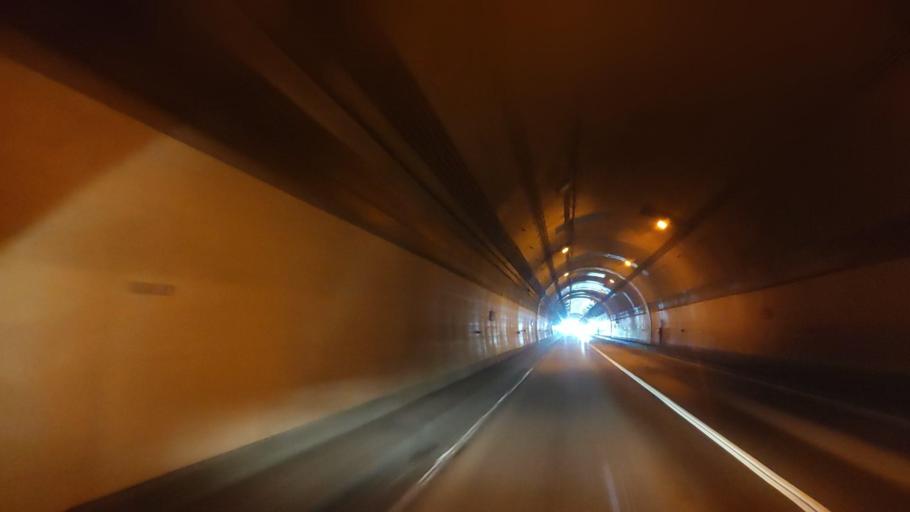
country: JP
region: Hokkaido
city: Rumoi
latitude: 43.8035
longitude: 141.3865
